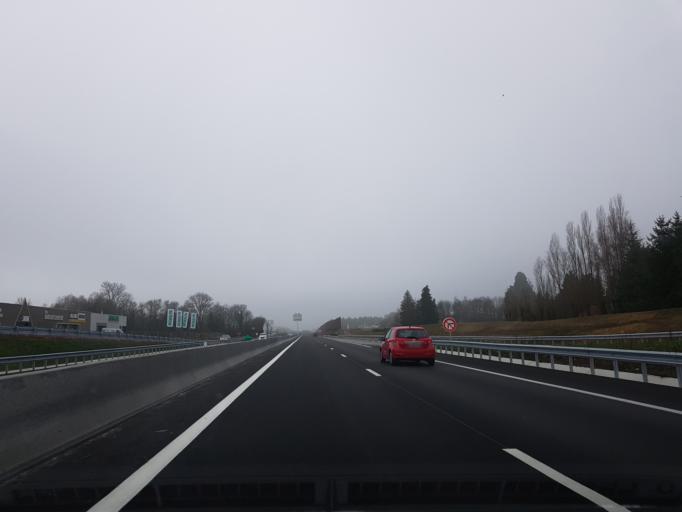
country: FR
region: Bourgogne
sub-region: Departement de Saone-et-Loire
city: Montchanin
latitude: 46.7358
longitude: 4.4783
